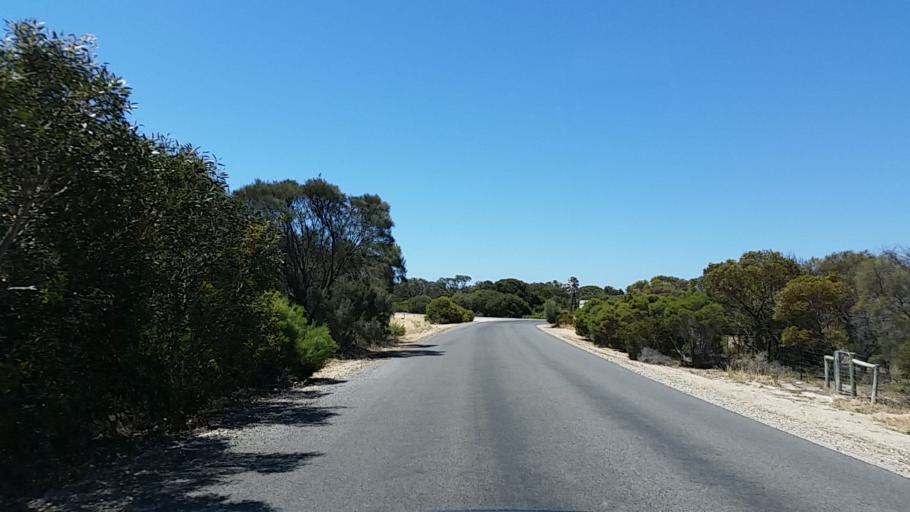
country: AU
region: South Australia
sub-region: Yorke Peninsula
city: Honiton
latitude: -35.2437
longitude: 136.9761
